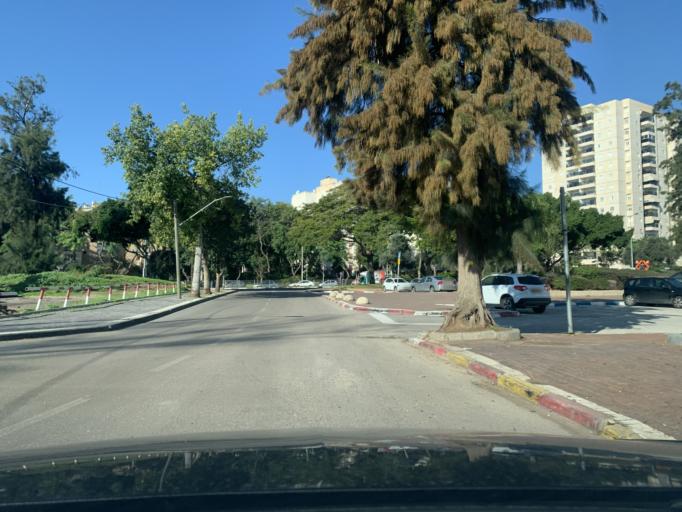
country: IL
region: Tel Aviv
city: Azor
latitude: 32.0462
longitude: 34.8145
